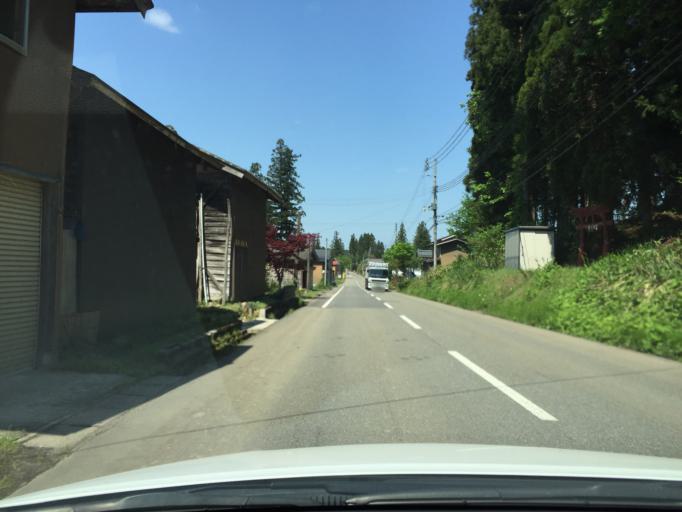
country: JP
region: Niigata
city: Tochio-honcho
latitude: 37.5042
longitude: 139.0656
